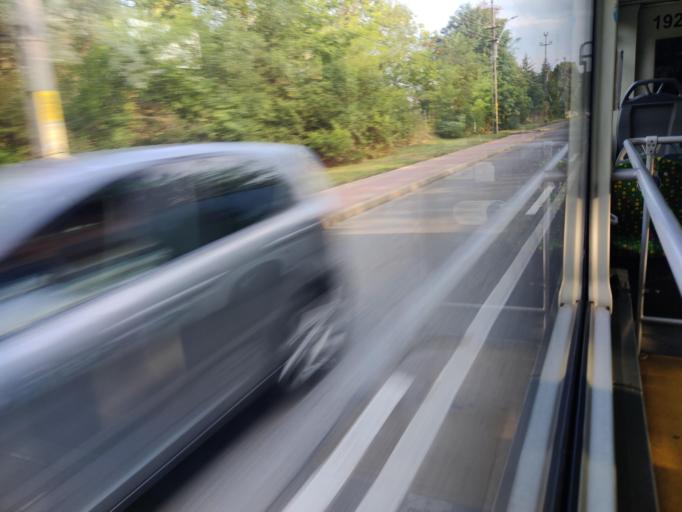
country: RO
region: Iasi
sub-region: Municipiul Iasi
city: Iasi
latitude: 47.1776
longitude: 27.5981
